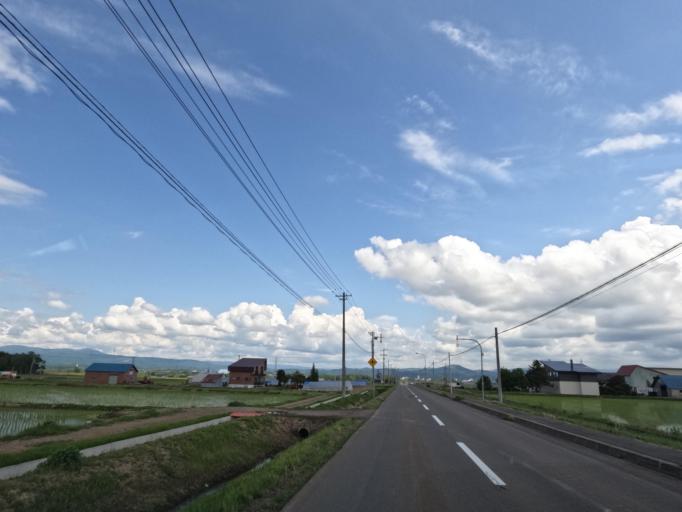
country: JP
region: Hokkaido
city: Takikawa
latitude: 43.5753
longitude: 141.8515
